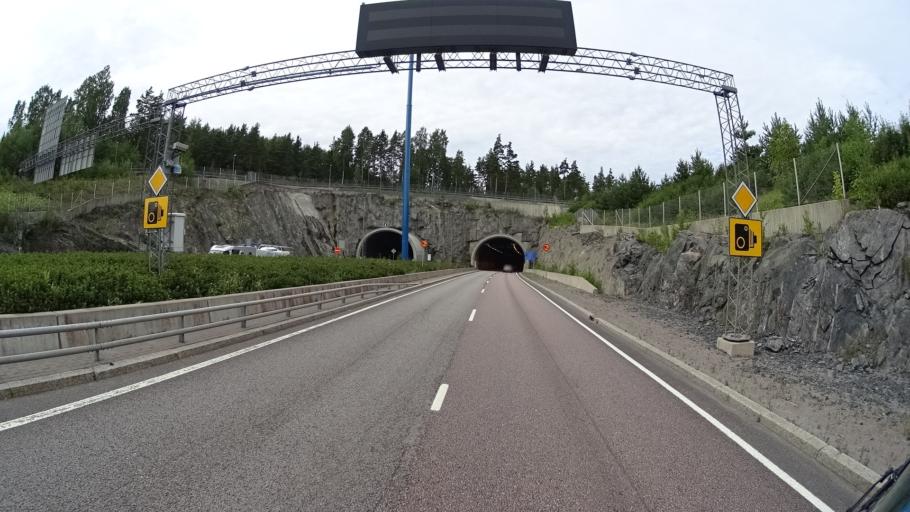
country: FI
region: Uusimaa
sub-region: Helsinki
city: Vantaa
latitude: 60.2264
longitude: 25.1675
